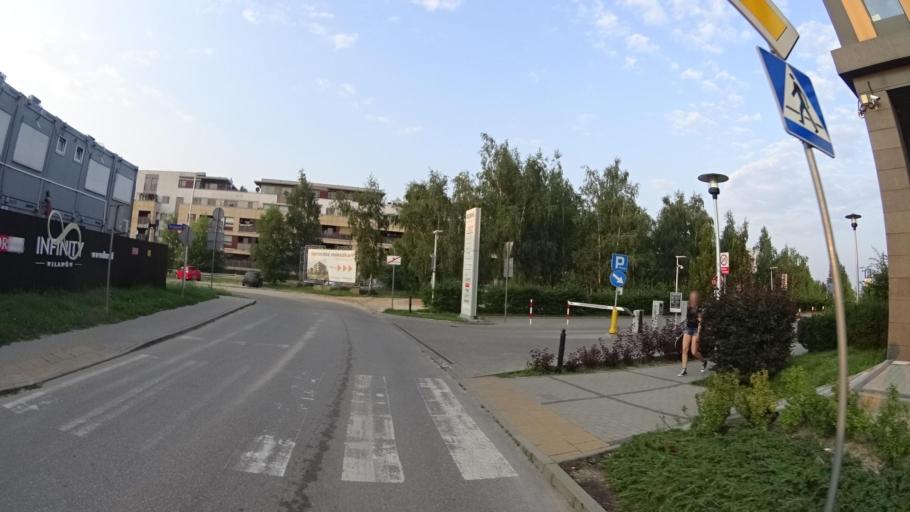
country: PL
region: Masovian Voivodeship
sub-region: Warszawa
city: Wilanow
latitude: 52.1544
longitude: 21.0811
